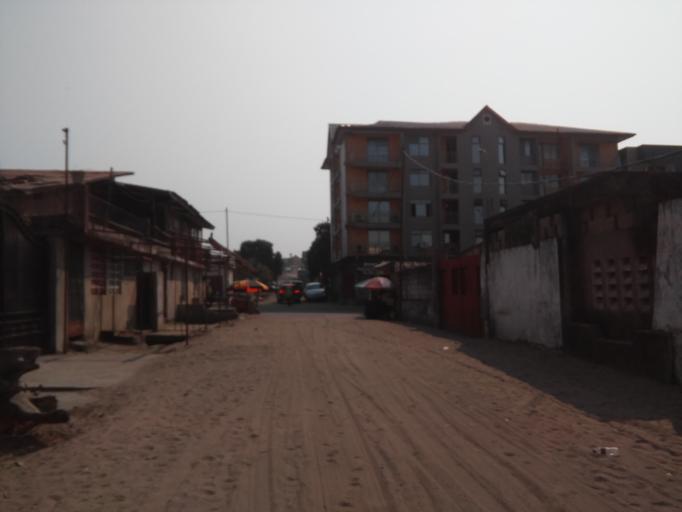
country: CD
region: Kinshasa
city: Kinshasa
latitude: -4.3428
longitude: 15.2669
